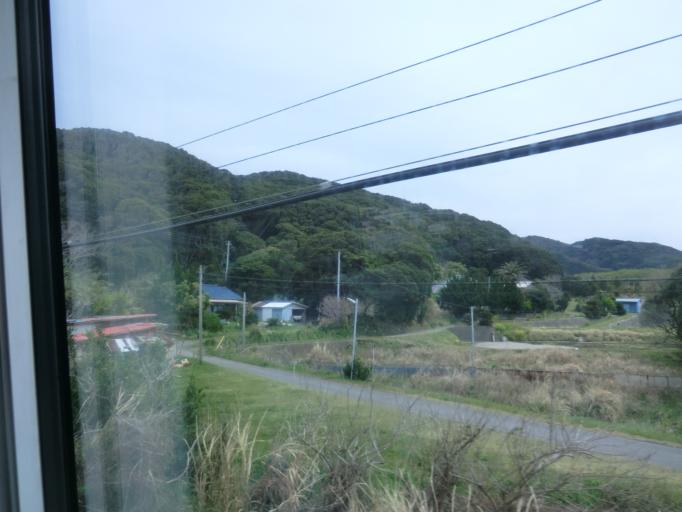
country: JP
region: Chiba
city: Futtsu
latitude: 35.1809
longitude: 139.8197
